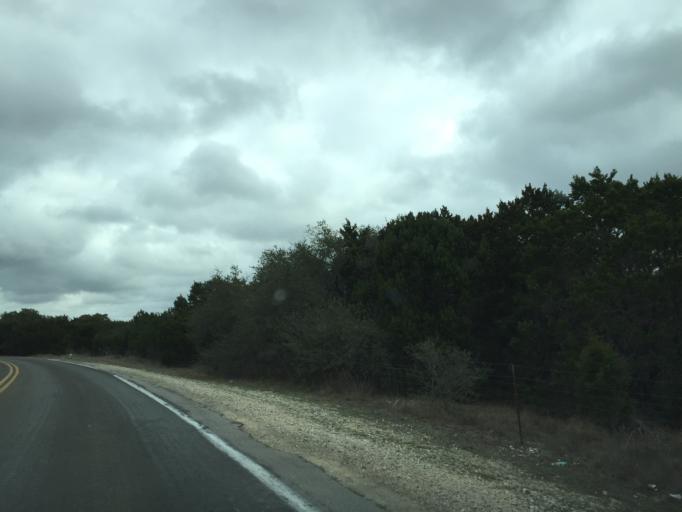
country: US
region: Texas
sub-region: Travis County
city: Hudson Bend
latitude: 30.4017
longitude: -97.8720
